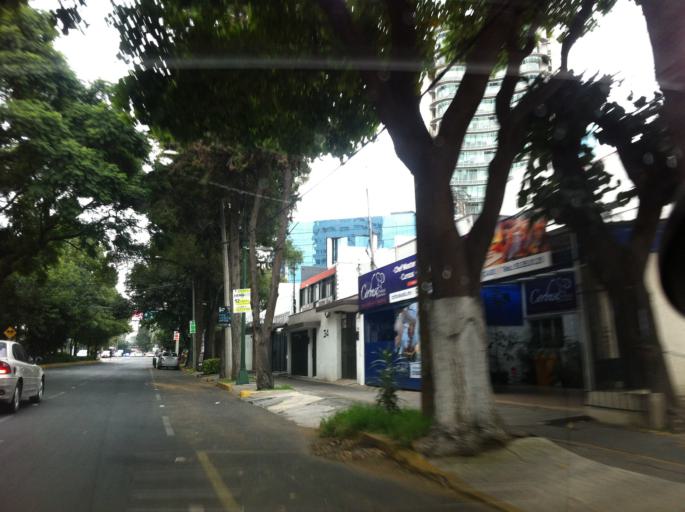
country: MX
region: Mexico City
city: Colonia del Valle
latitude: 19.3807
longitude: -99.1755
